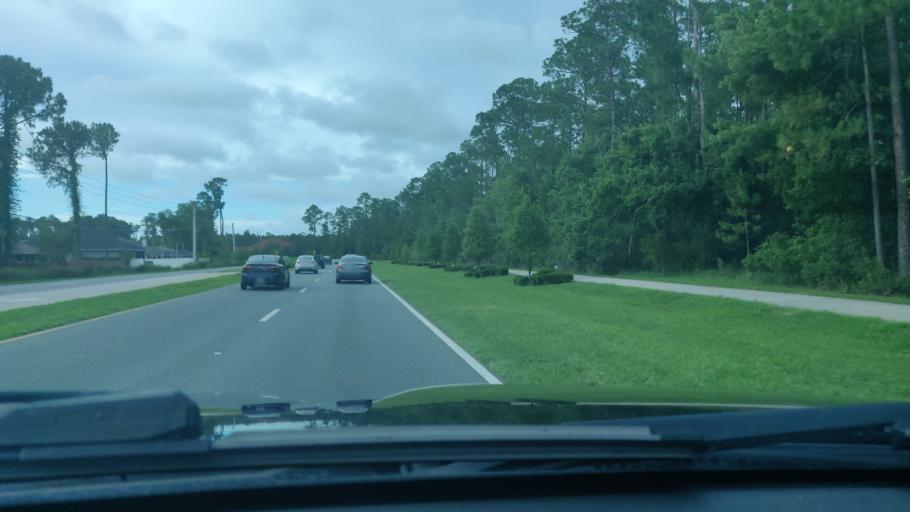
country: US
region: Florida
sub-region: Flagler County
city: Bunnell
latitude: 29.4913
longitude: -81.2206
